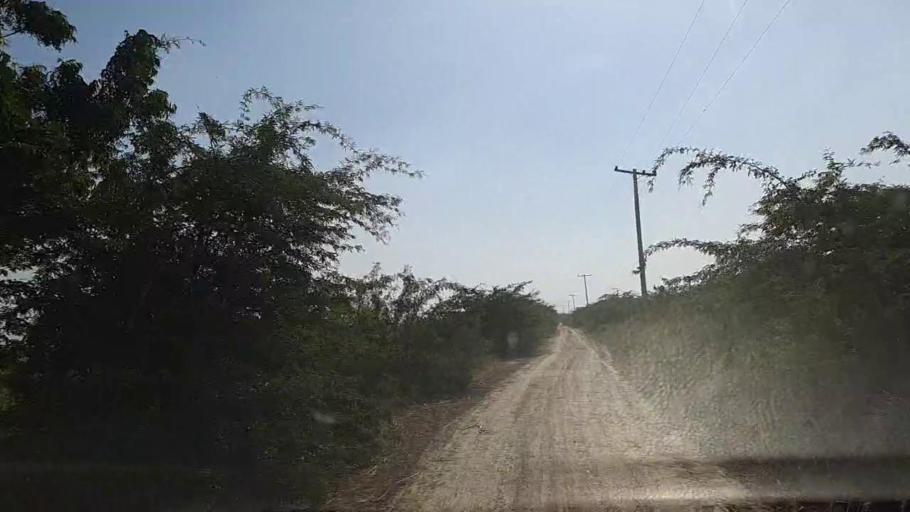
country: PK
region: Sindh
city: Daro Mehar
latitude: 24.7761
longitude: 68.0682
